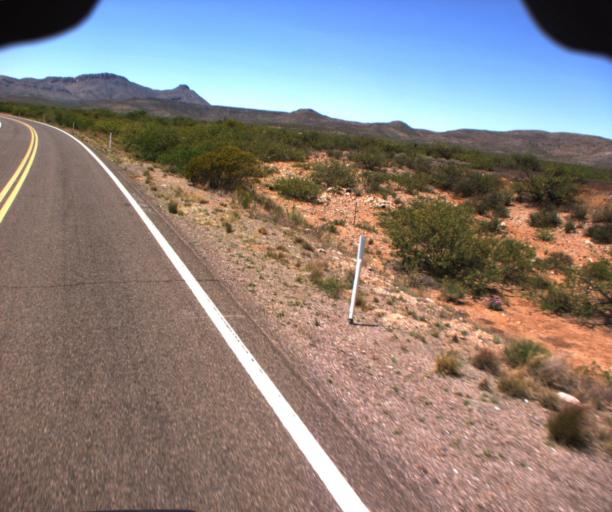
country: US
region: Arizona
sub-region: Cochise County
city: Douglas
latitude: 31.4949
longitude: -109.3357
